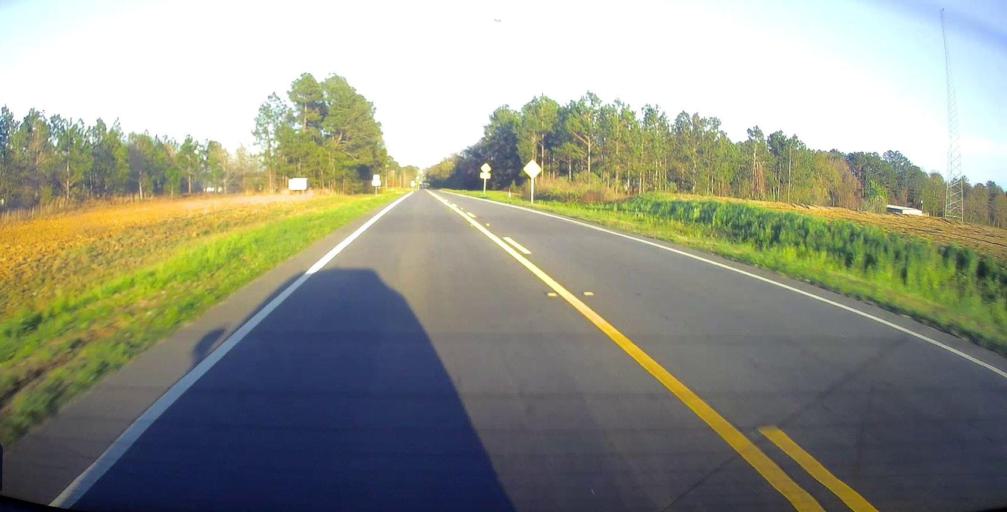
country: US
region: Georgia
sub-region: Wilcox County
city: Rochelle
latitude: 31.9496
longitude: -83.4871
